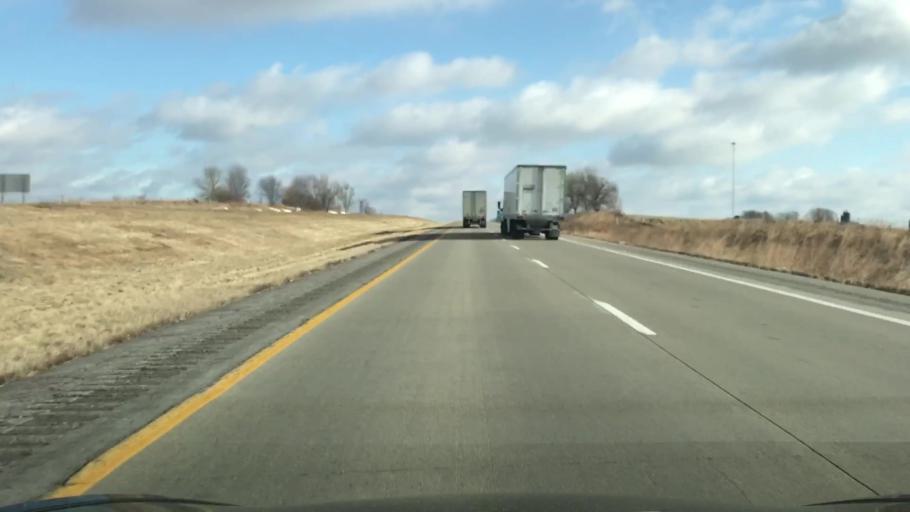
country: US
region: Iowa
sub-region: Cass County
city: Atlantic
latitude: 41.4972
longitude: -94.9748
